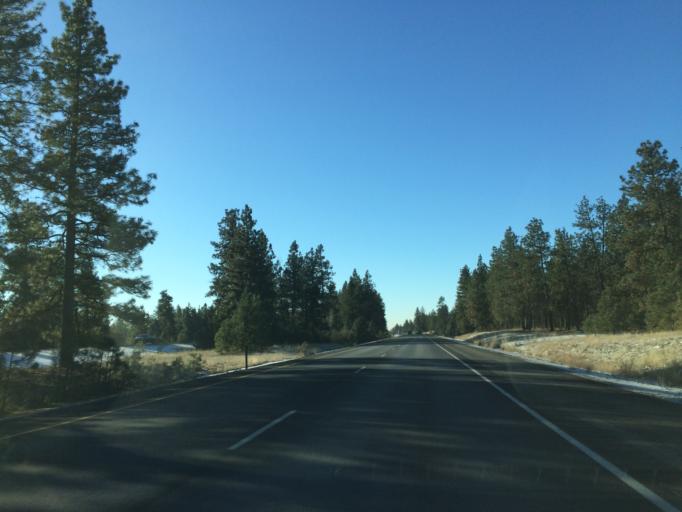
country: US
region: Washington
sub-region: Spokane County
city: Medical Lake
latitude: 47.4254
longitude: -117.8044
